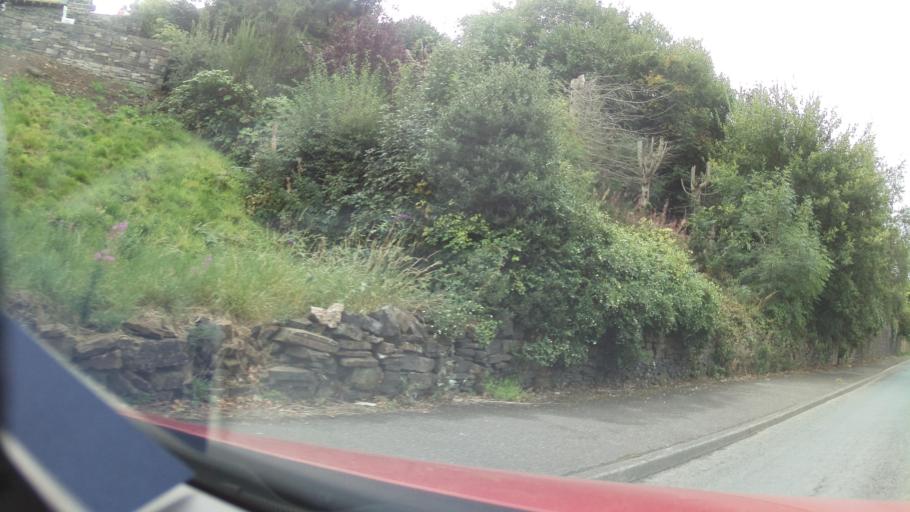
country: GB
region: England
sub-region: Kirklees
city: Holmfirth
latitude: 53.5768
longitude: -1.7793
